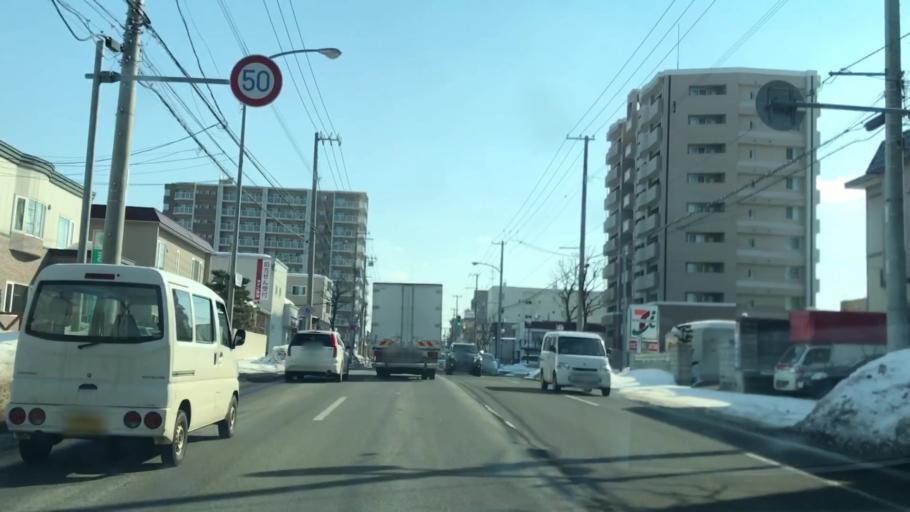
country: JP
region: Hokkaido
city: Sapporo
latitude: 43.0240
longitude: 141.3884
